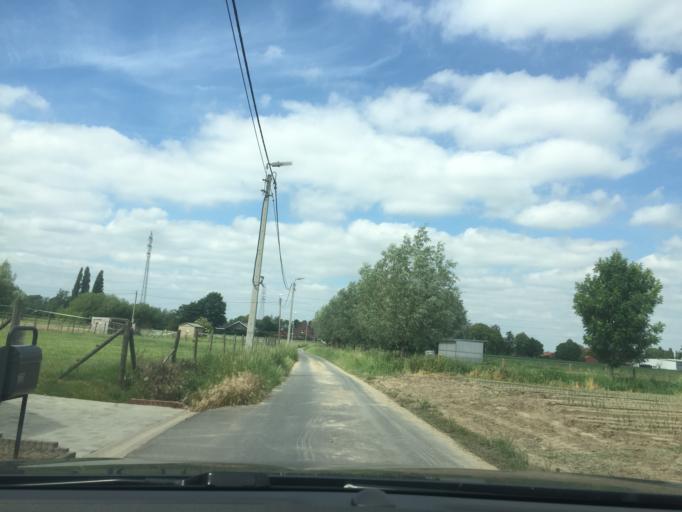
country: BE
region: Flanders
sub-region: Provincie West-Vlaanderen
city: Izegem
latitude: 50.8977
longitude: 3.2156
